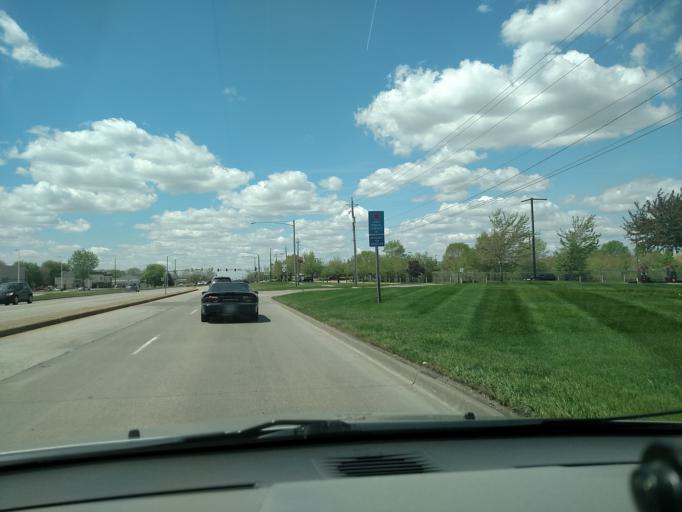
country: US
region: Iowa
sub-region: Polk County
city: Ankeny
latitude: 41.7029
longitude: -93.5816
